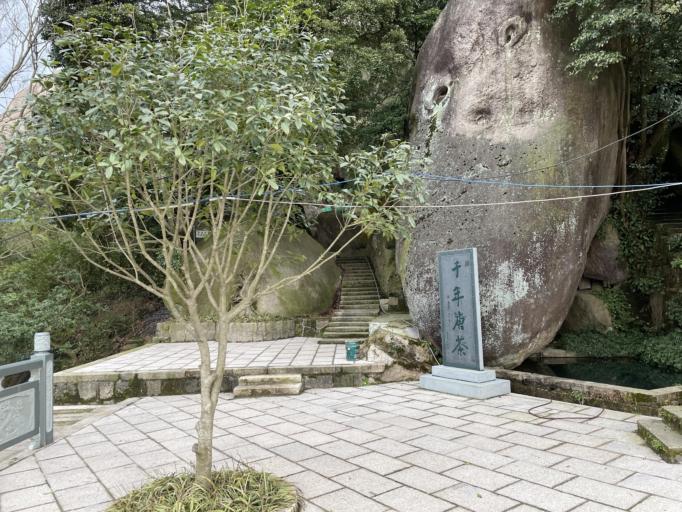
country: CN
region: Zhejiang Sheng
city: Wenzhou
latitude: 27.8732
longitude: 120.7179
